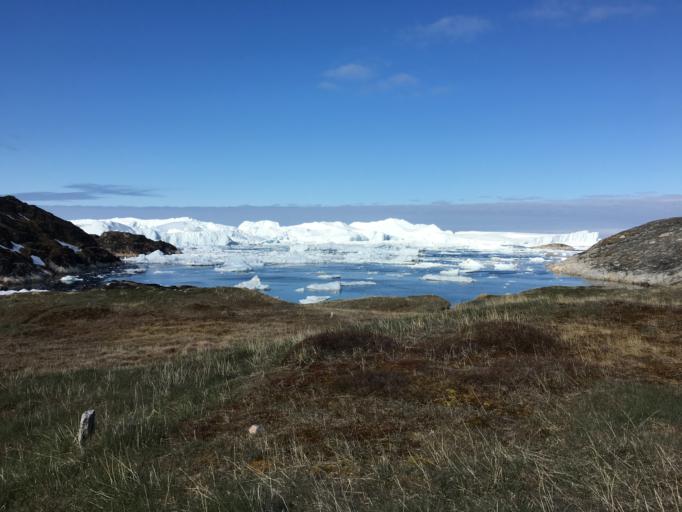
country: GL
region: Qaasuitsup
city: Ilulissat
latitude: 69.2019
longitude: -51.1256
